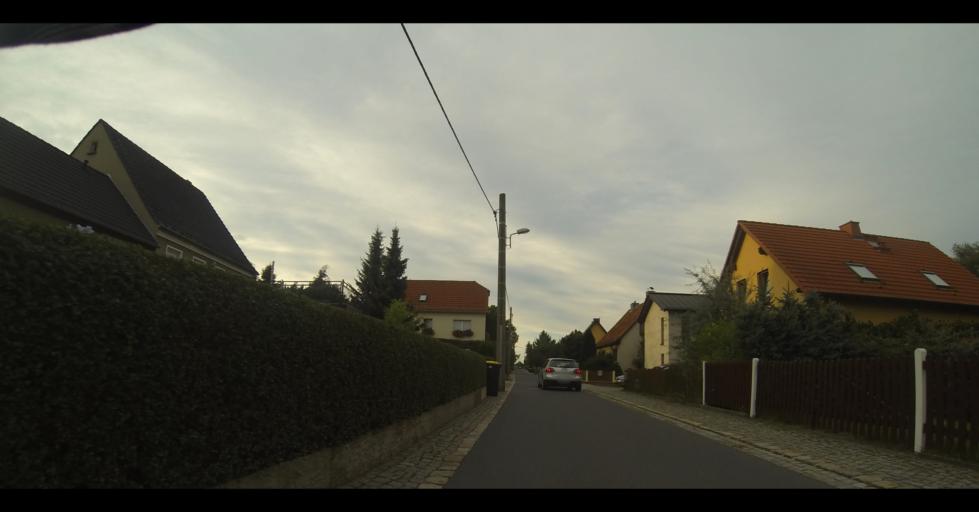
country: DE
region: Saxony
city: Radeburg
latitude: 51.1975
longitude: 13.7265
